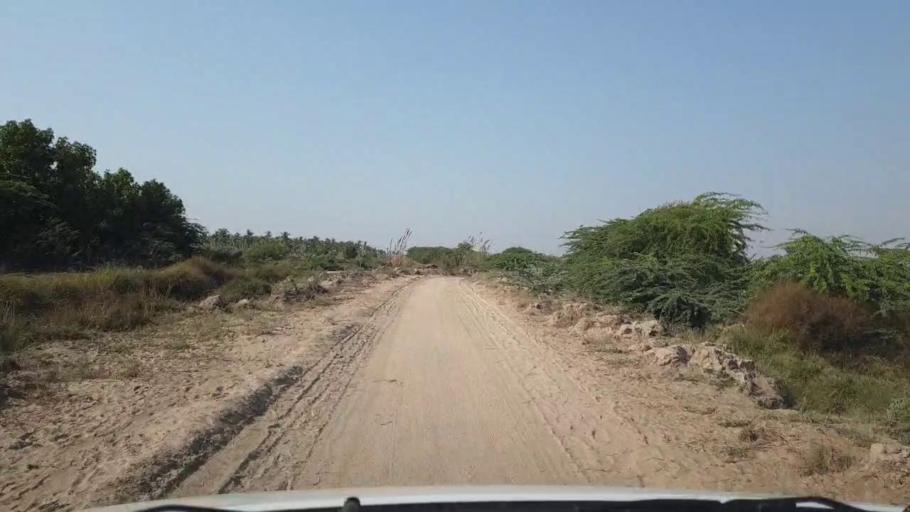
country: PK
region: Sindh
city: Mirpur Sakro
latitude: 24.5937
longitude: 67.6302
